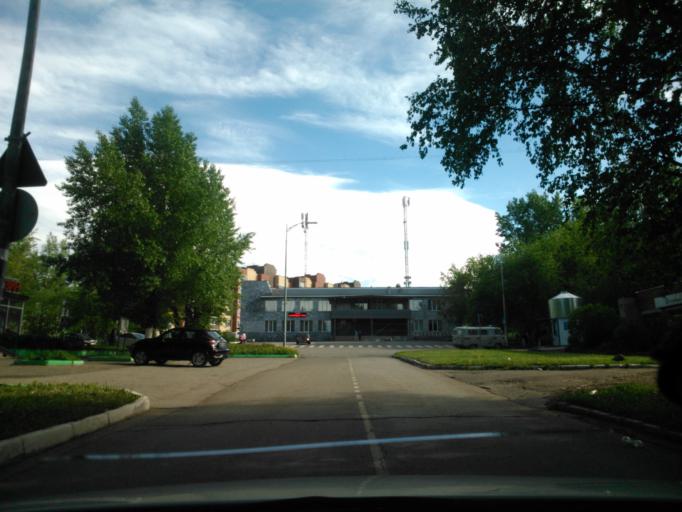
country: RU
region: Perm
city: Lobanovo
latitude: 57.8627
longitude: 56.2884
